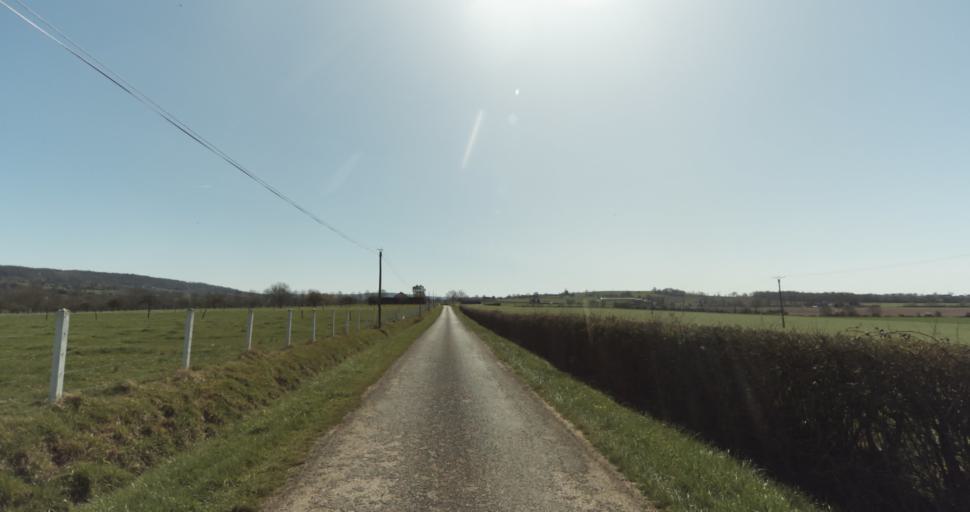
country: FR
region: Lower Normandy
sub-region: Departement du Calvados
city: Saint-Pierre-sur-Dives
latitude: 49.0008
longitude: 0.0221
